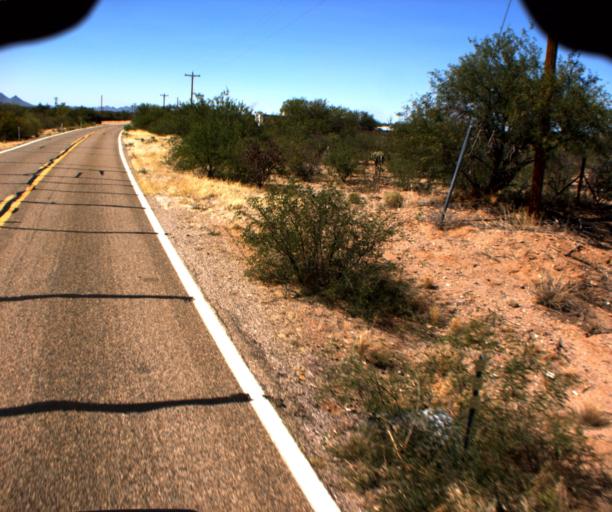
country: US
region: Arizona
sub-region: Pima County
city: Three Points
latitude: 31.8803
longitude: -111.3961
